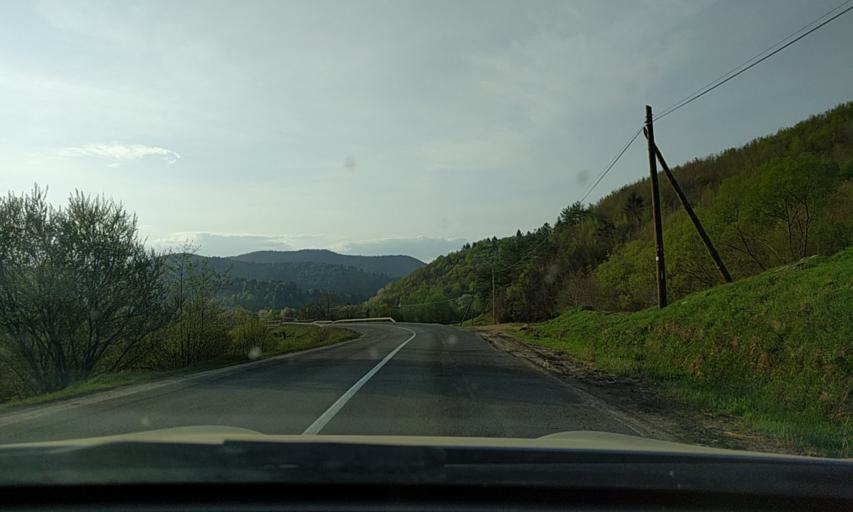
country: RO
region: Covasna
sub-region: Comuna Bretcu
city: Bretcu
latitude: 46.0471
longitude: 26.3207
